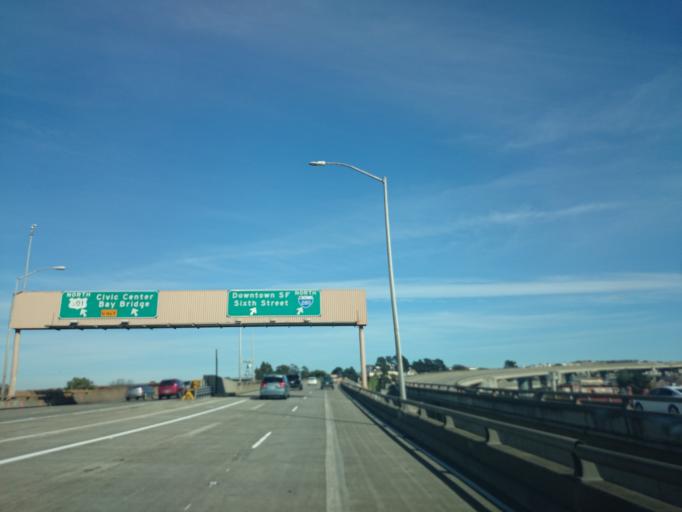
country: US
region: California
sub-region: San Francisco County
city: San Francisco
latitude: 37.7339
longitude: -122.4102
